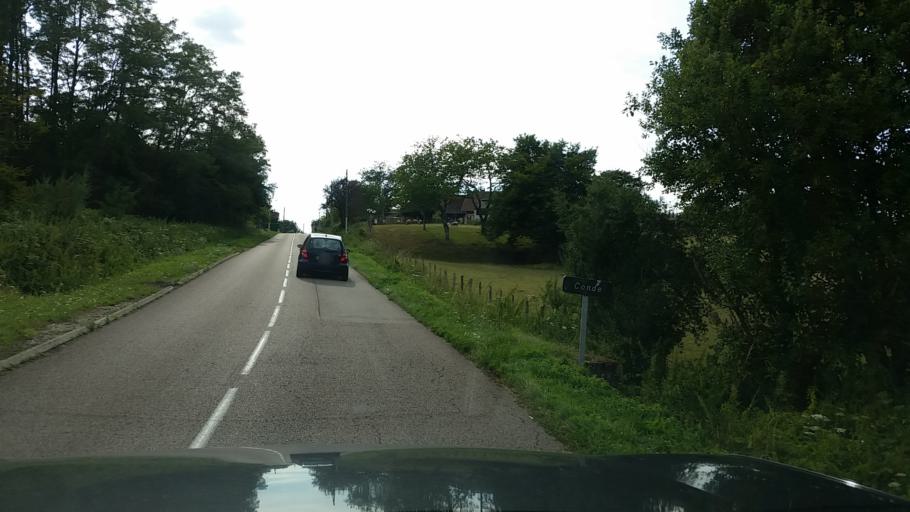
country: FR
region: Bourgogne
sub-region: Departement de Saone-et-Loire
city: Saint-Germain-du-Bois
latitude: 46.7319
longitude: 5.2810
